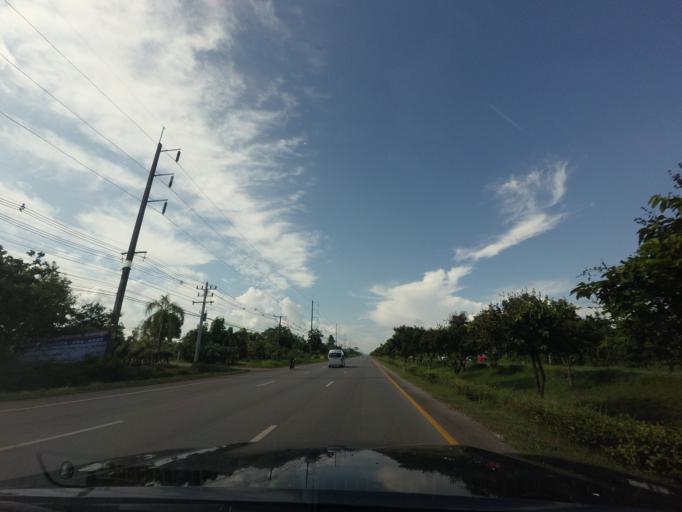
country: TH
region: Nong Khai
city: Nong Khai
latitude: 17.7896
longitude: 102.7637
